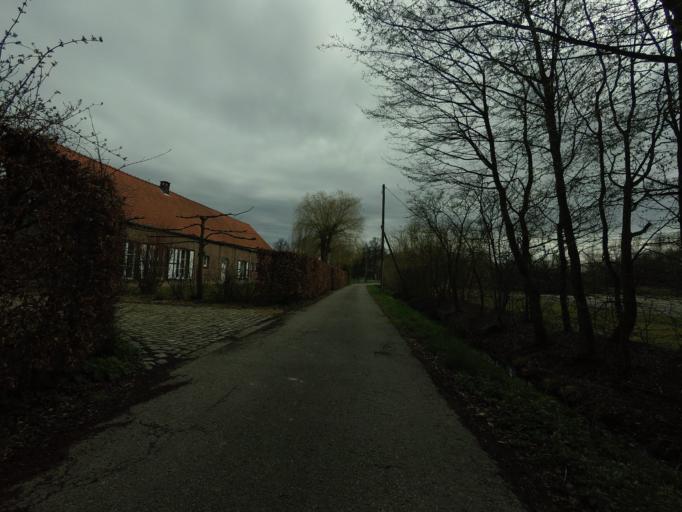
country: BE
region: Flanders
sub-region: Provincie Antwerpen
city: Boechout
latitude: 51.1500
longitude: 4.5057
